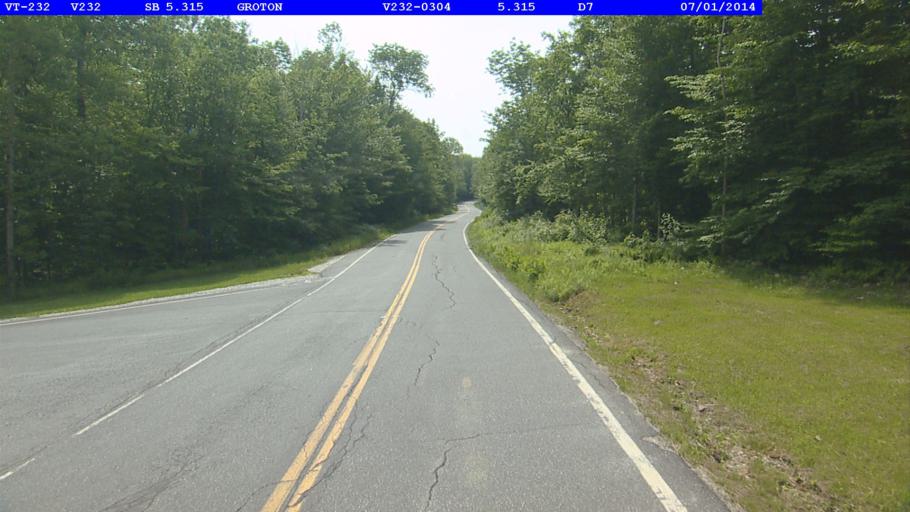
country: US
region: Vermont
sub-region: Washington County
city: Barre
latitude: 44.2763
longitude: -72.2842
